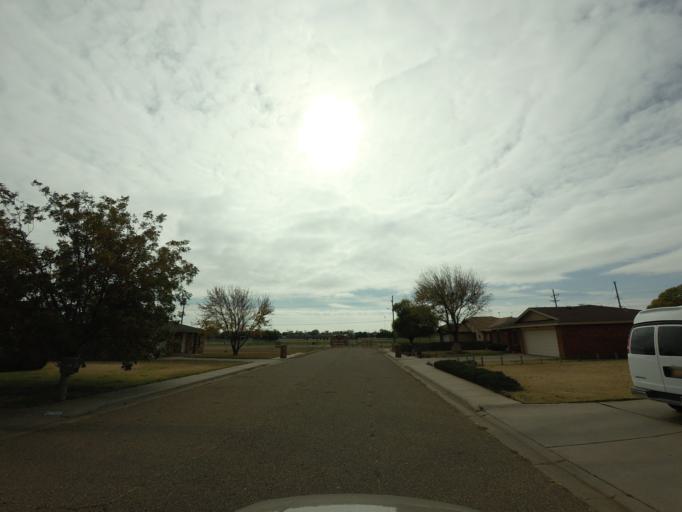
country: US
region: New Mexico
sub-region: Curry County
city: Clovis
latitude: 34.4272
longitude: -103.2289
